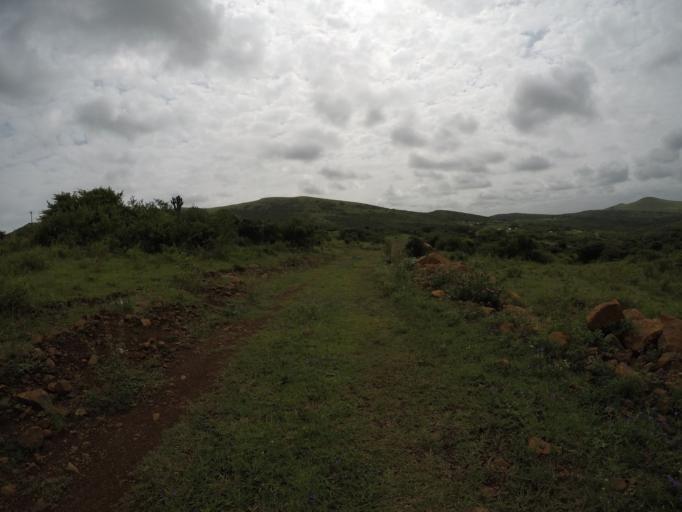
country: ZA
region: KwaZulu-Natal
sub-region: uThungulu District Municipality
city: Empangeni
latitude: -28.6137
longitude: 31.8997
